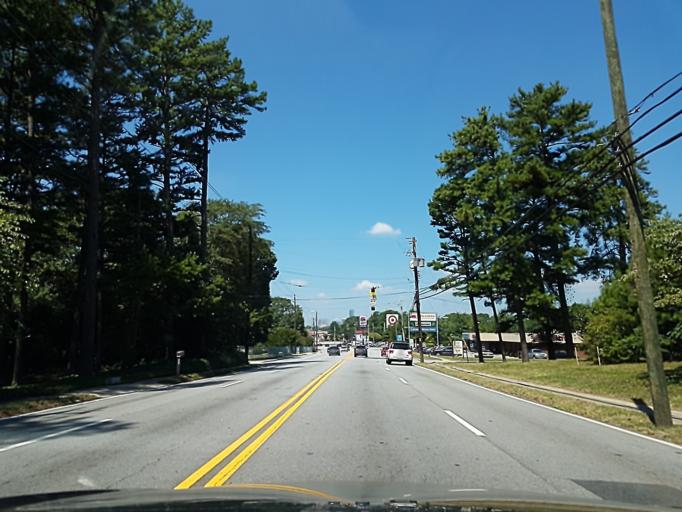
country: US
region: Georgia
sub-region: DeKalb County
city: North Druid Hills
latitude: 33.8258
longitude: -84.3233
